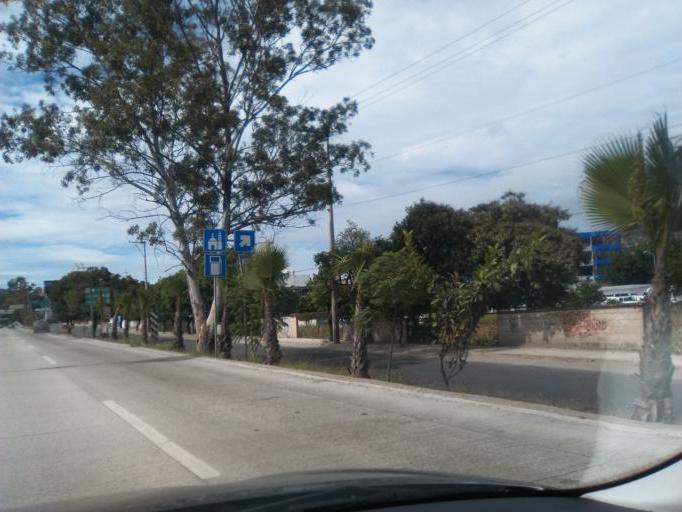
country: MX
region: Guerrero
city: Chilpancingo de los Bravos
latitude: 17.5395
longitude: -99.5010
